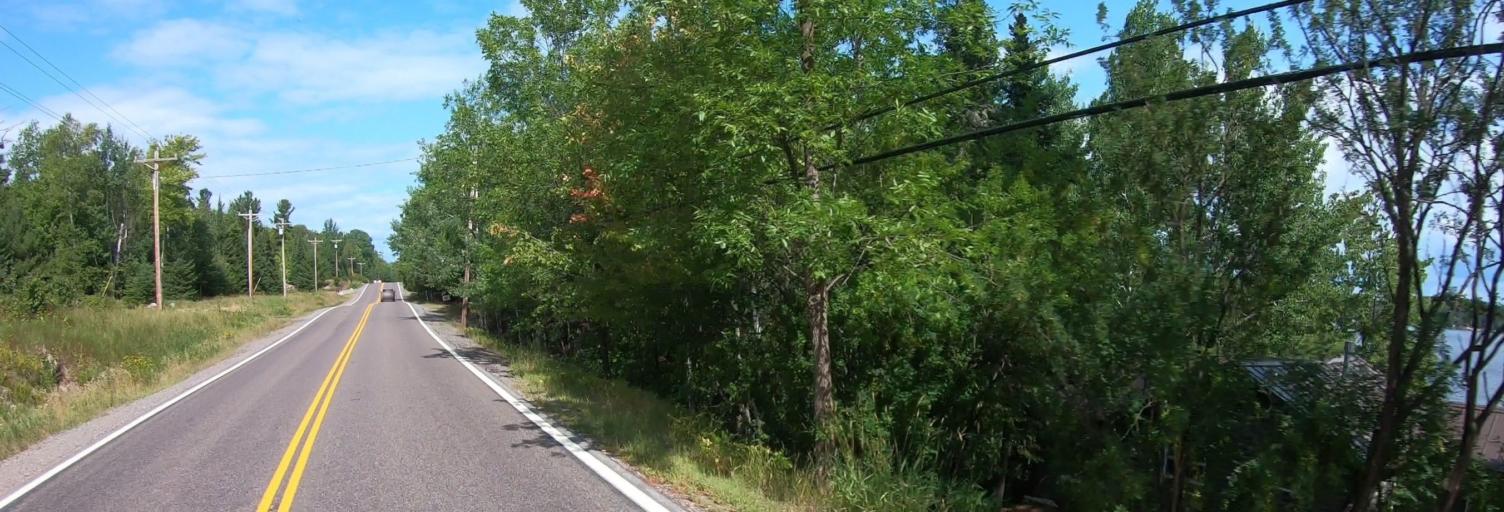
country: US
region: Minnesota
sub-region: Saint Louis County
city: Mountain Iron
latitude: 47.9294
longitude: -92.6698
